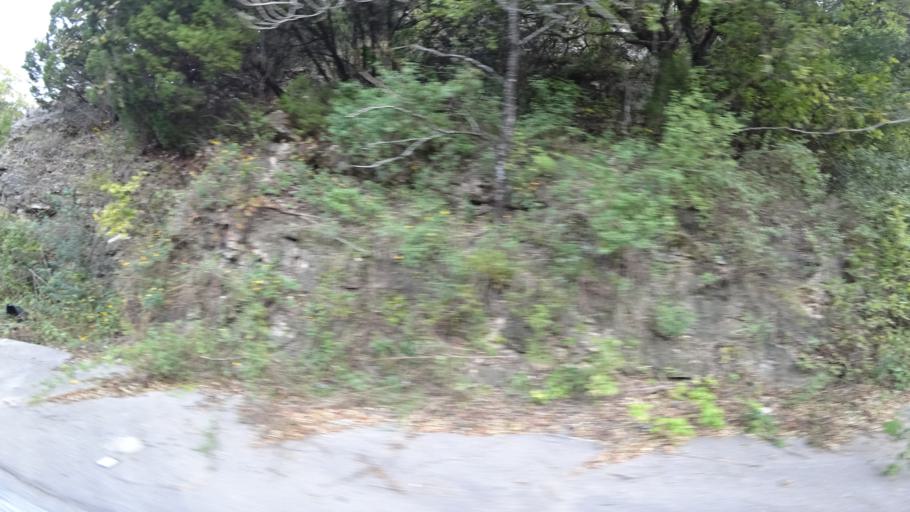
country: US
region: Texas
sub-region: Travis County
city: West Lake Hills
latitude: 30.2916
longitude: -97.7891
